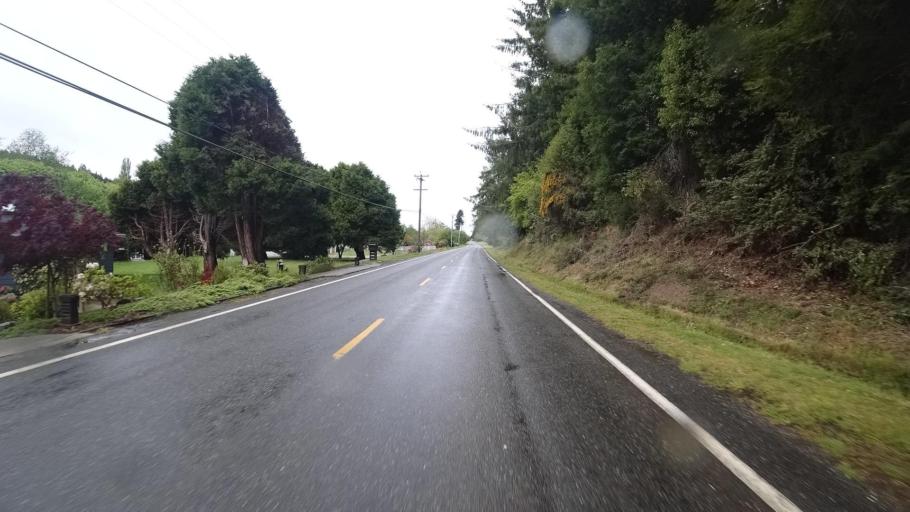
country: US
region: California
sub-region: Humboldt County
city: Bayside
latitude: 40.8339
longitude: -124.0456
